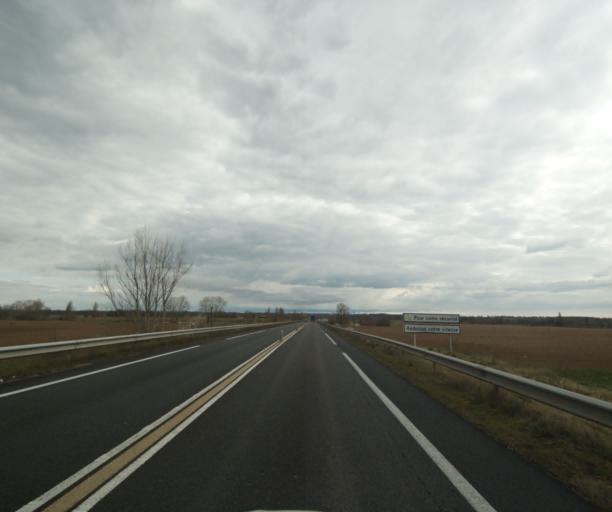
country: FR
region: Auvergne
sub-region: Departement de l'Allier
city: Toulon-sur-Allier
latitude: 46.4808
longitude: 3.3309
